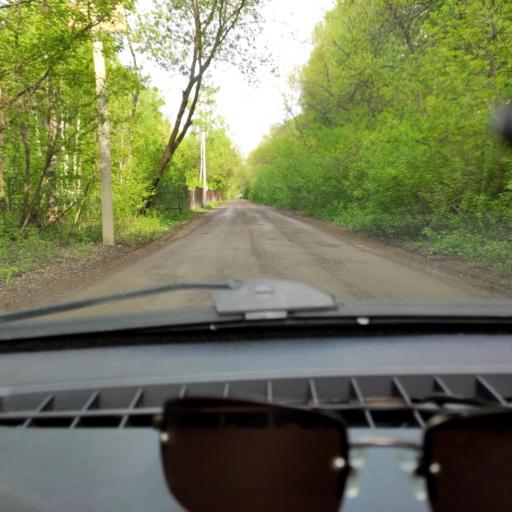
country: RU
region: Bashkortostan
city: Ufa
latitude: 54.6979
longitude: 55.9355
